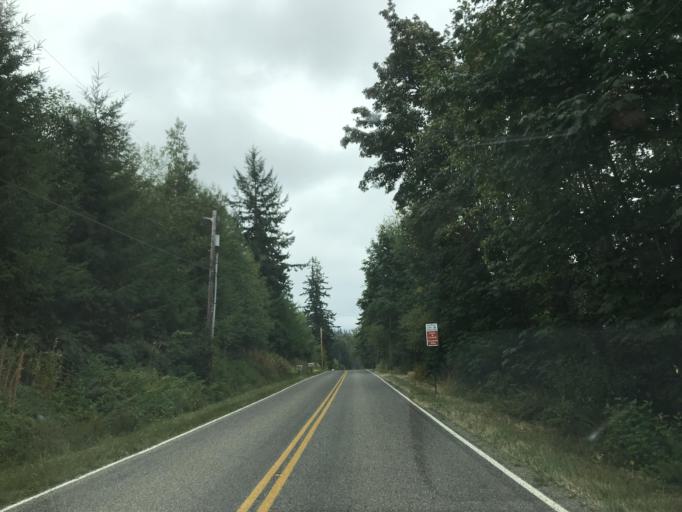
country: US
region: Washington
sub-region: Whatcom County
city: Sudden Valley
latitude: 48.7793
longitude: -122.3332
